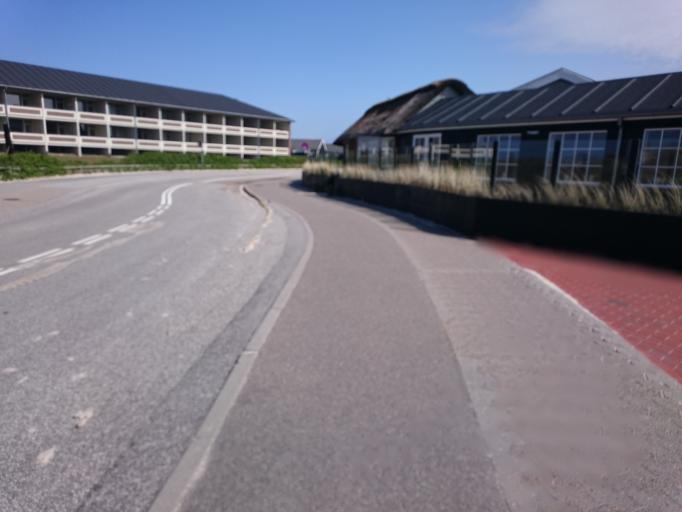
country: DK
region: South Denmark
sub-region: Fano Kommune
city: Nordby
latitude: 55.4330
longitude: 8.3649
